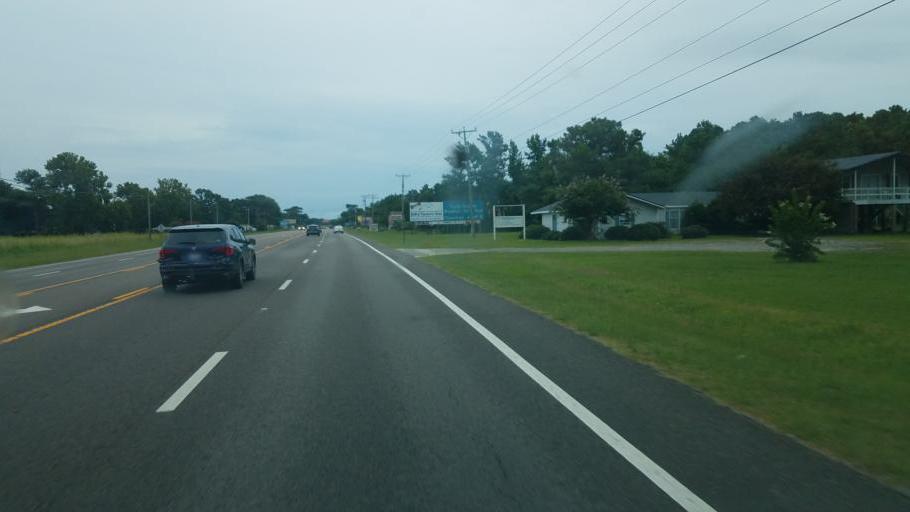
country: US
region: North Carolina
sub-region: Dare County
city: Southern Shores
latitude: 36.1736
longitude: -75.8620
